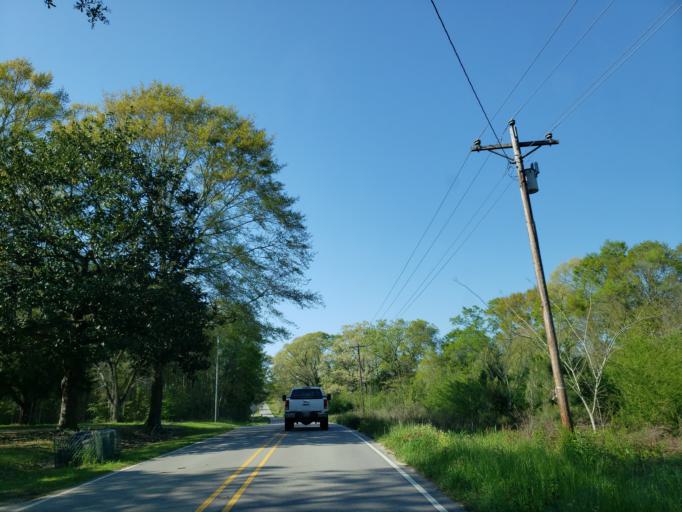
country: US
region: Mississippi
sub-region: Covington County
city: Collins
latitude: 31.6142
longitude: -89.3881
